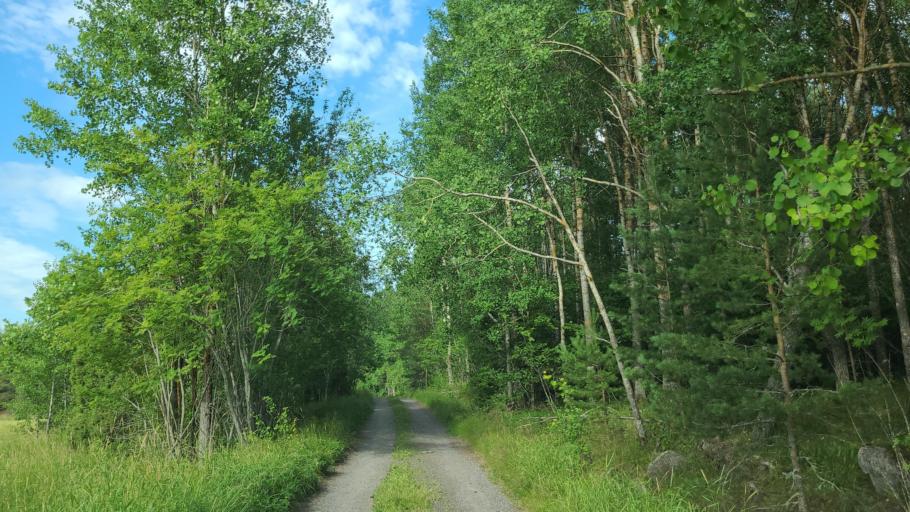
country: FI
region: Varsinais-Suomi
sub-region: Turku
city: Rymaettylae
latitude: 60.2891
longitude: 21.9654
